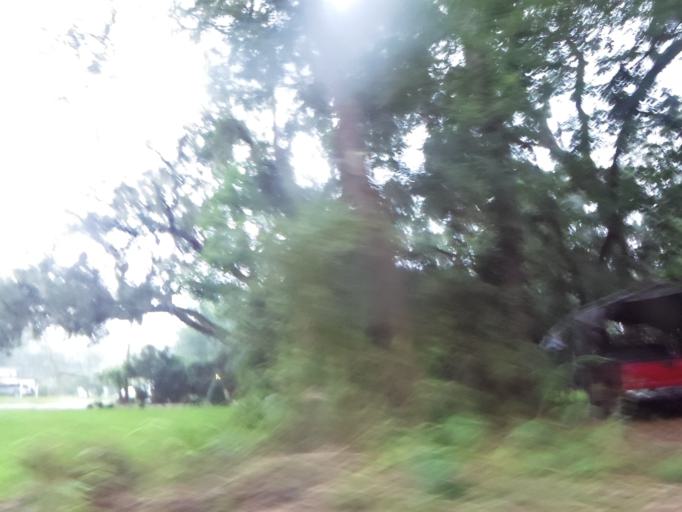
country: US
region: Florida
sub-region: Duval County
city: Jacksonville
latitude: 30.3430
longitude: -81.6055
